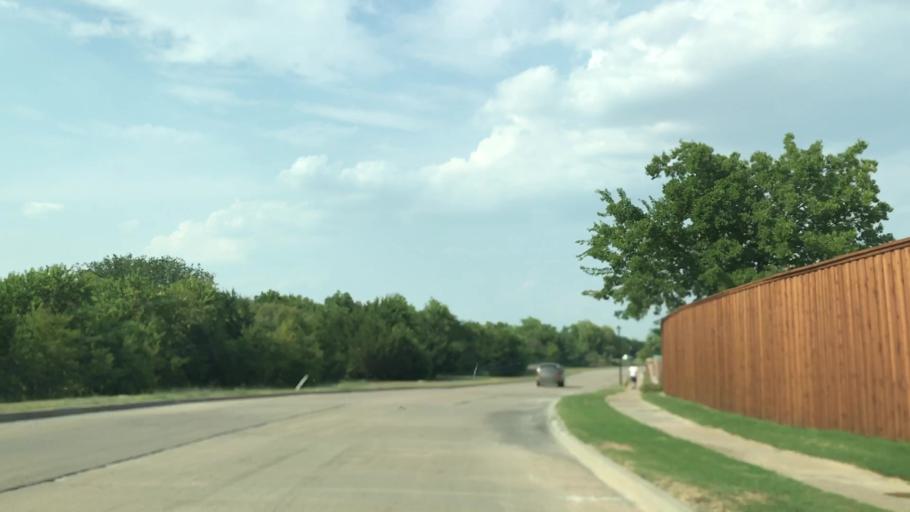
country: US
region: Texas
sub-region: Rockwall County
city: Rockwall
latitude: 32.8971
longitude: -96.4396
